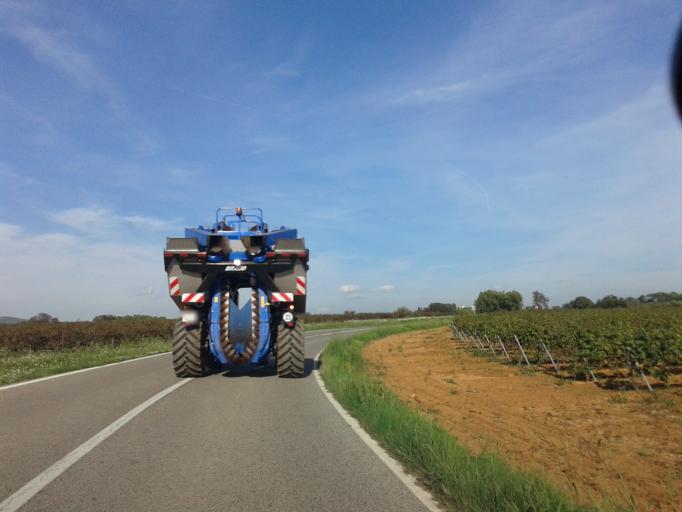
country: ES
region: Catalonia
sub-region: Provincia de Tarragona
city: Sant Jaume dels Domenys
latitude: 41.3157
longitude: 1.5843
